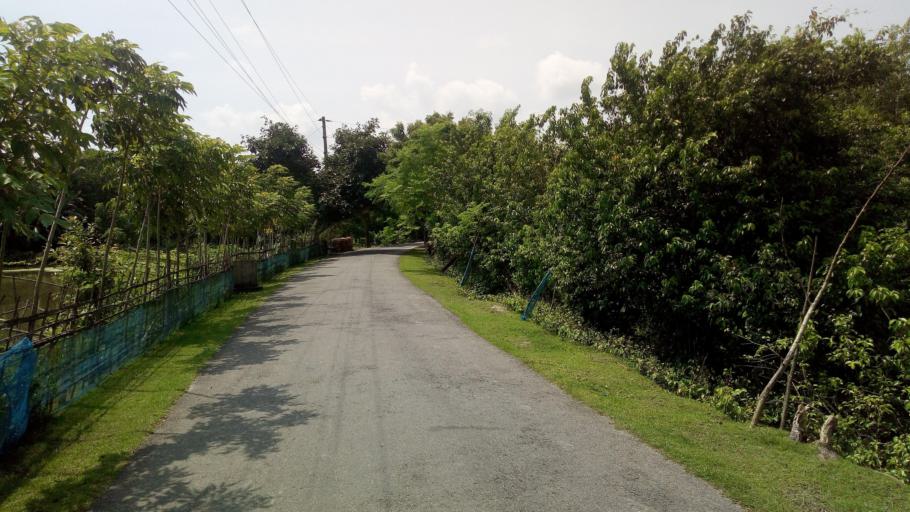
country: BD
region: Khulna
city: Phultala
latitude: 22.5798
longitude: 89.4530
